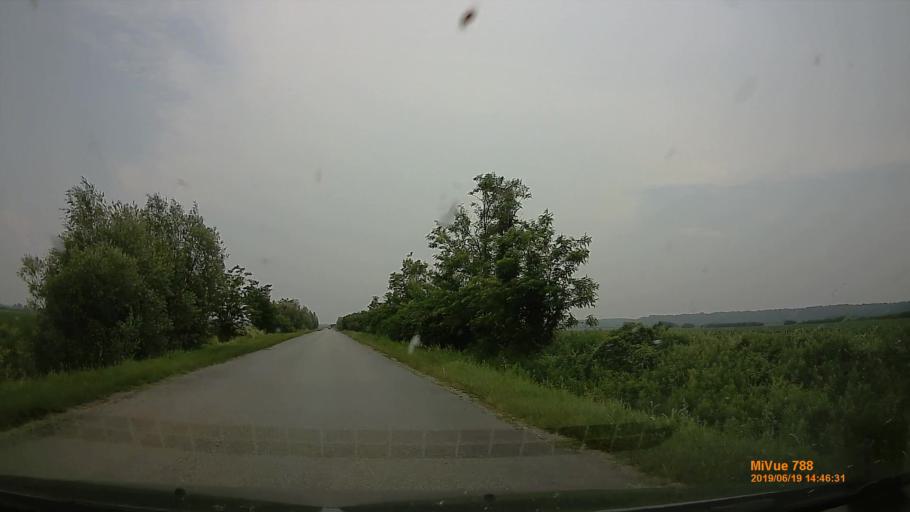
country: HU
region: Baranya
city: Szigetvar
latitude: 46.0059
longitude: 17.8247
